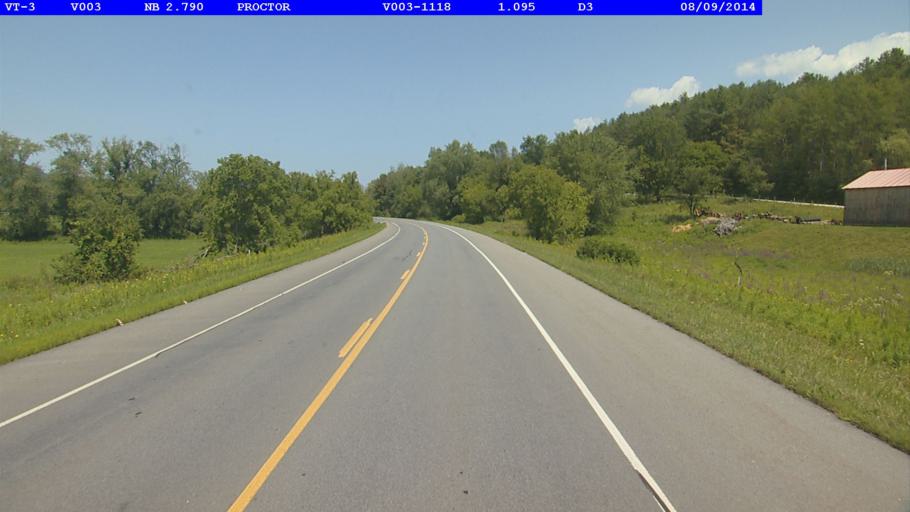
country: US
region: Vermont
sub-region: Rutland County
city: West Rutland
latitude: 43.6396
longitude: -73.0326
